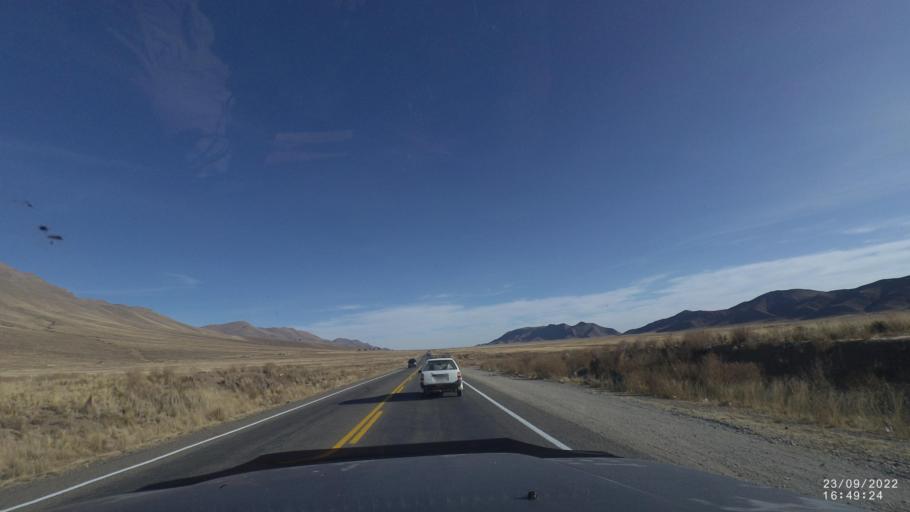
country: BO
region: Oruro
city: Poopo
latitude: -18.3885
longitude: -66.9786
